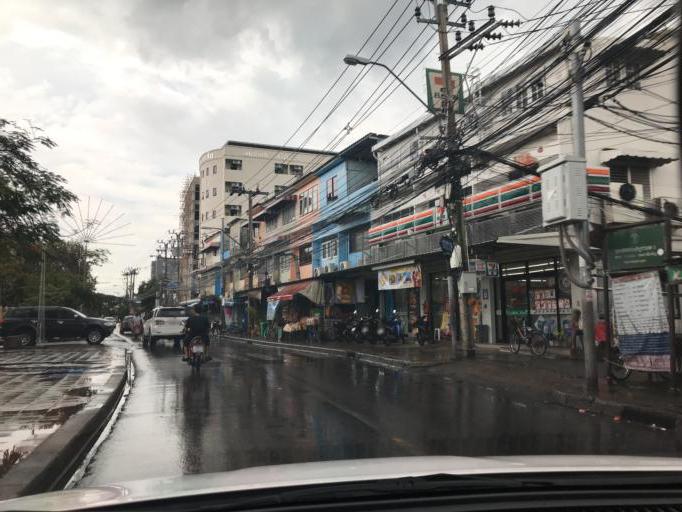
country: TH
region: Bangkok
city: Phasi Charoen
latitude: 13.7193
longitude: 100.4422
